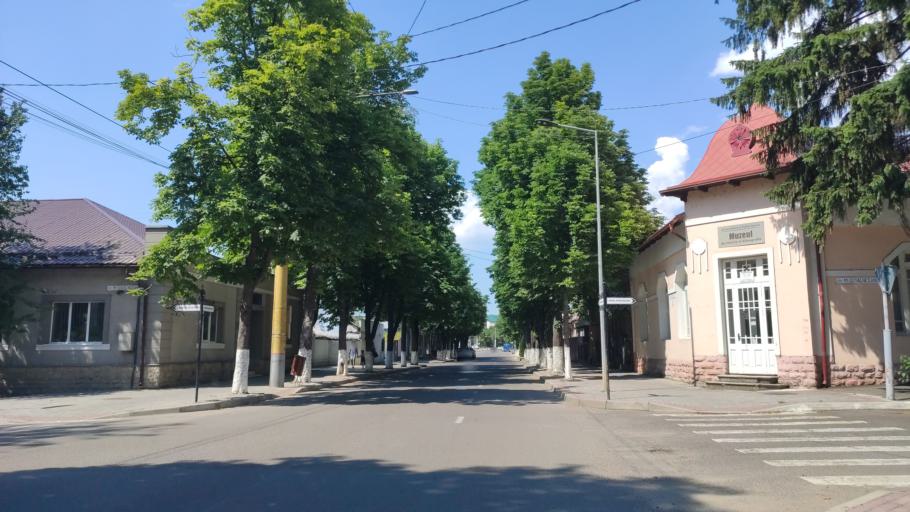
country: MD
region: Raionul Soroca
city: Soroca
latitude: 48.1550
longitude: 28.3020
